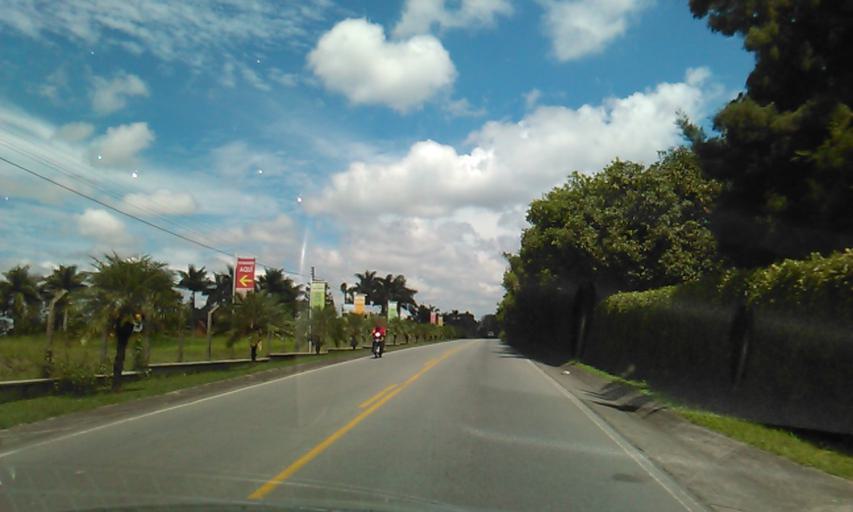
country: CO
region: Quindio
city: Armenia
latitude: 4.4722
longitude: -75.7034
